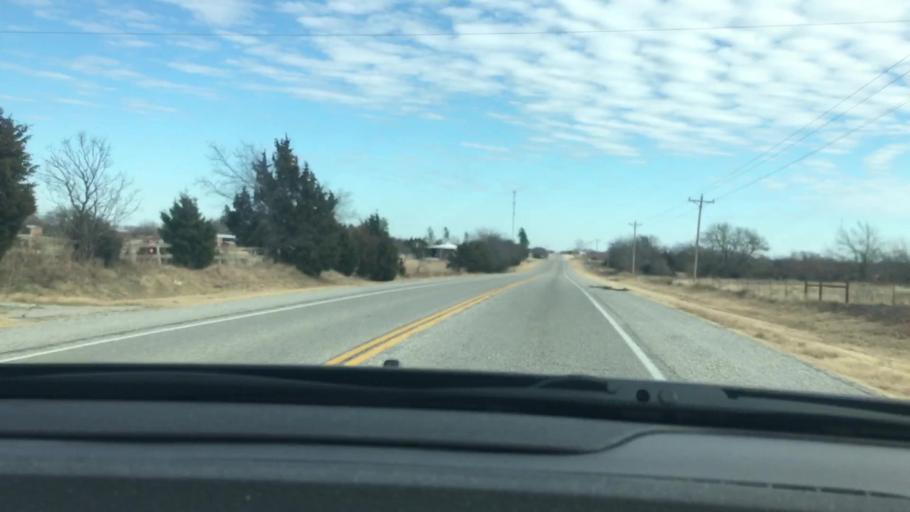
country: US
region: Oklahoma
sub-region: Garvin County
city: Stratford
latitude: 34.7965
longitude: -97.0599
